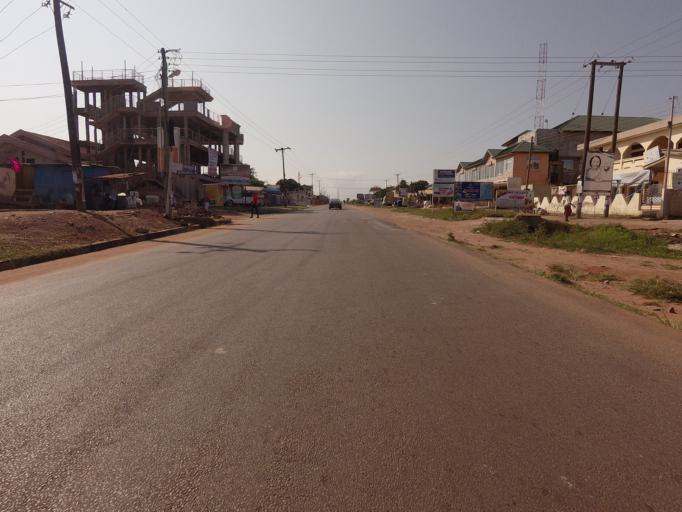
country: GH
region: Greater Accra
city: Teshi Old Town
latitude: 5.6035
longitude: -0.1045
